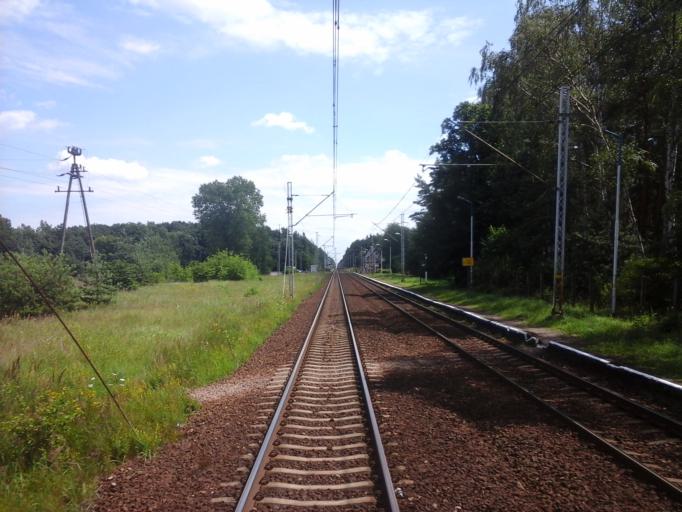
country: PL
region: West Pomeranian Voivodeship
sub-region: Powiat gryfinski
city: Stare Czarnowo
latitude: 53.3834
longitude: 14.7614
